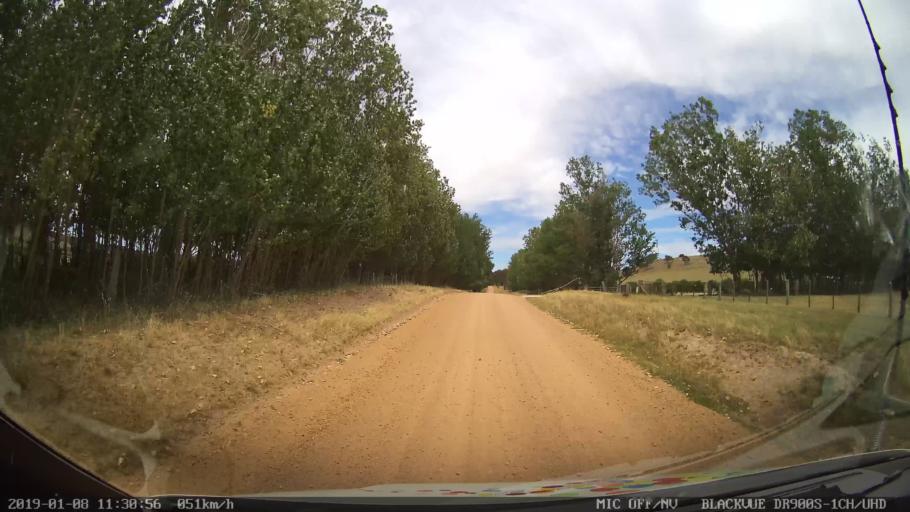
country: AU
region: New South Wales
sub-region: Guyra
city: Guyra
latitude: -30.3102
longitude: 151.5414
